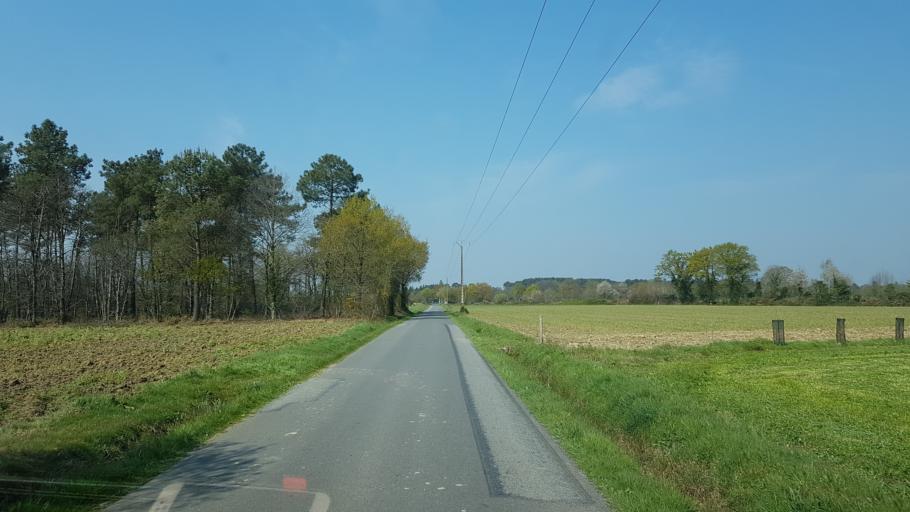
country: FR
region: Brittany
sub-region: Departement du Morbihan
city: Peaule
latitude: 47.5867
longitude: -2.3844
